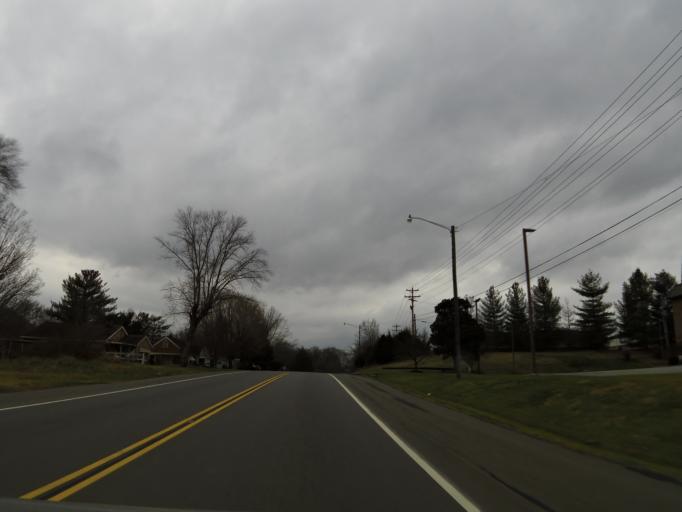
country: US
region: Tennessee
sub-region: Grainger County
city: Rutledge
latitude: 36.2824
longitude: -83.5090
